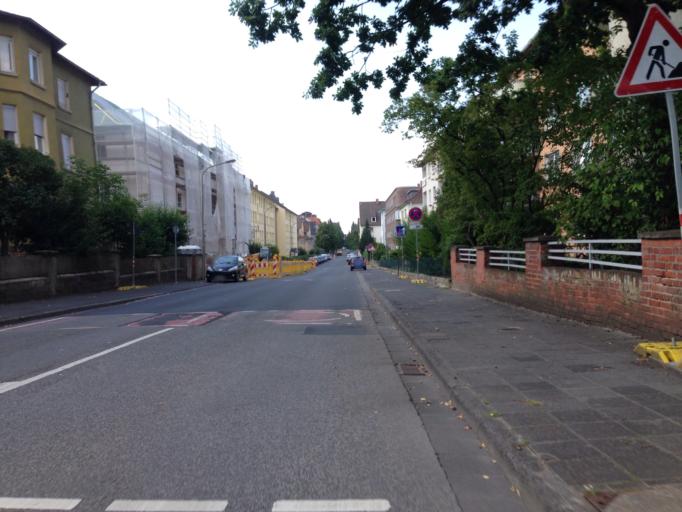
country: DE
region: Hesse
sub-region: Regierungsbezirk Giessen
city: Giessen
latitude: 50.5746
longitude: 8.6767
